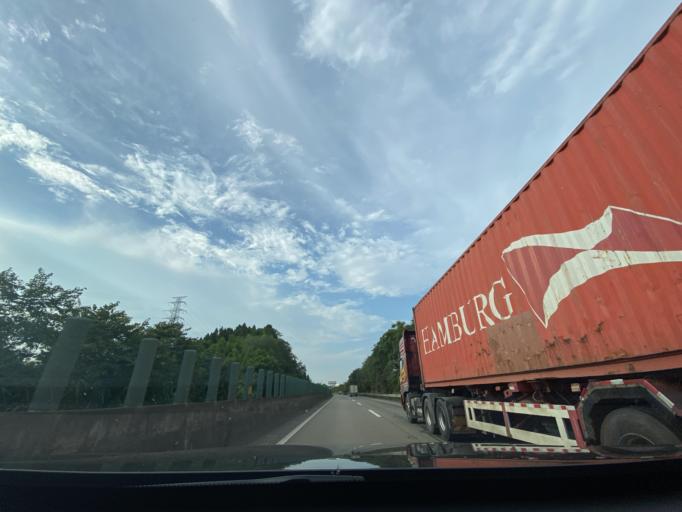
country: CN
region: Sichuan
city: Yanjiang
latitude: 30.0686
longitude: 104.5985
